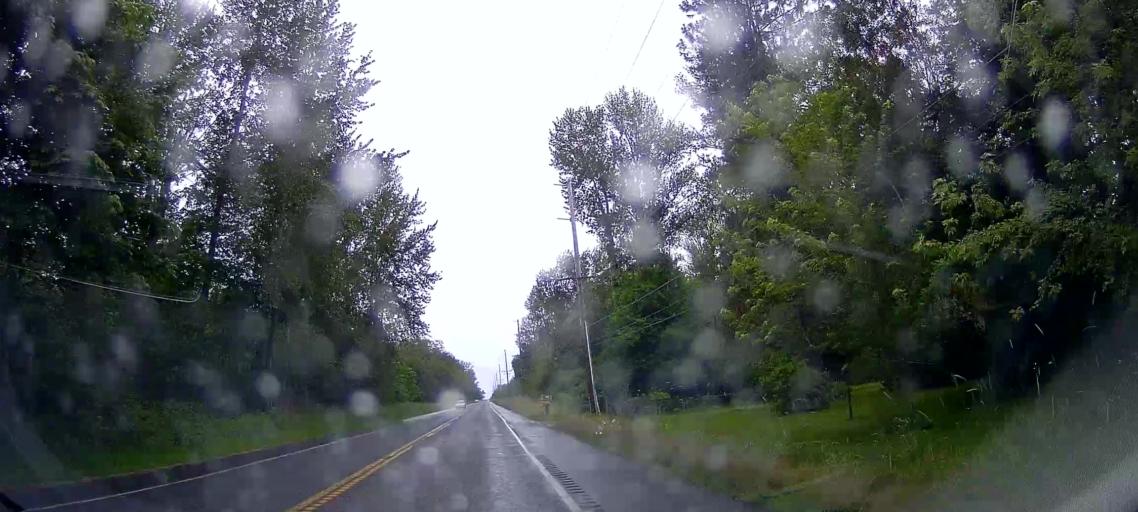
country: US
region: Washington
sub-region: Whatcom County
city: Ferndale
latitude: 48.8196
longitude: -122.6724
